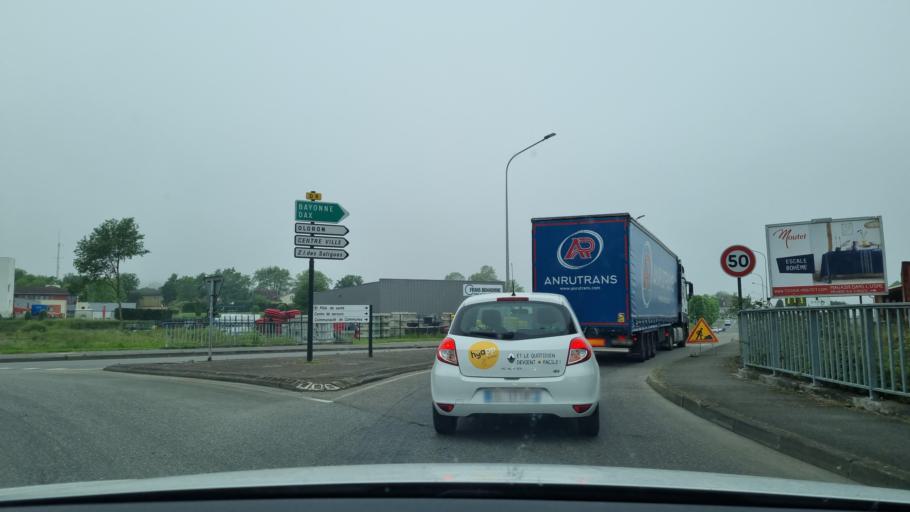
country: FR
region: Aquitaine
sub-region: Departement des Pyrenees-Atlantiques
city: Orthez
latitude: 43.4777
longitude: -0.7621
